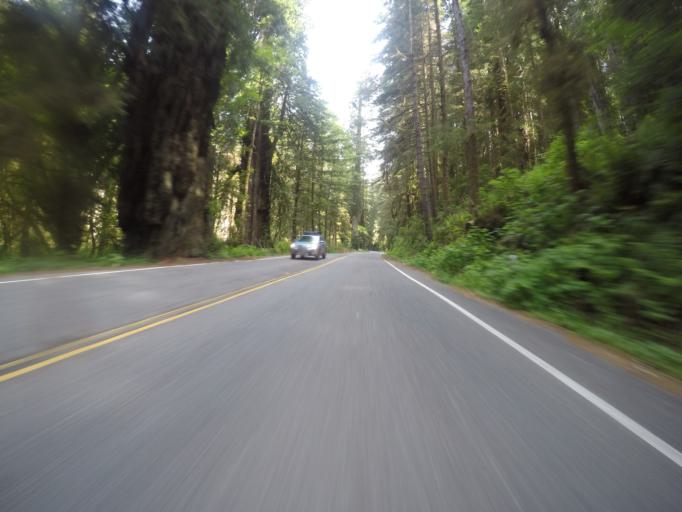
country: US
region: California
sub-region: Del Norte County
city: Bertsch-Oceanview
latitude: 41.4190
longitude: -124.0339
